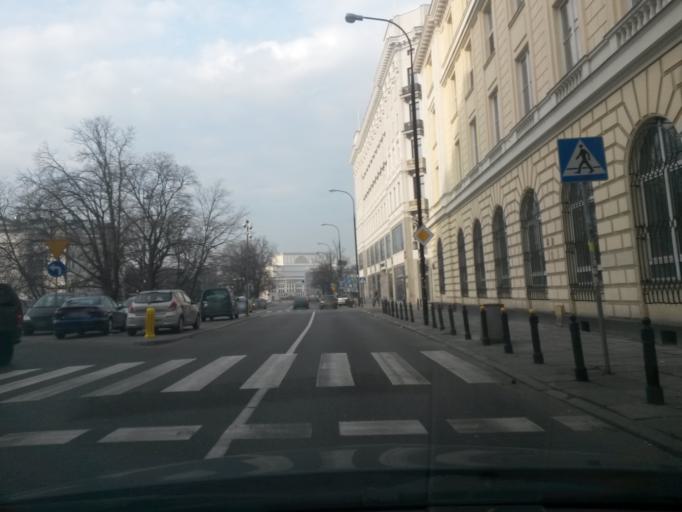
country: PL
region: Masovian Voivodeship
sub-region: Warszawa
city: Warsaw
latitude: 52.2382
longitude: 21.0129
